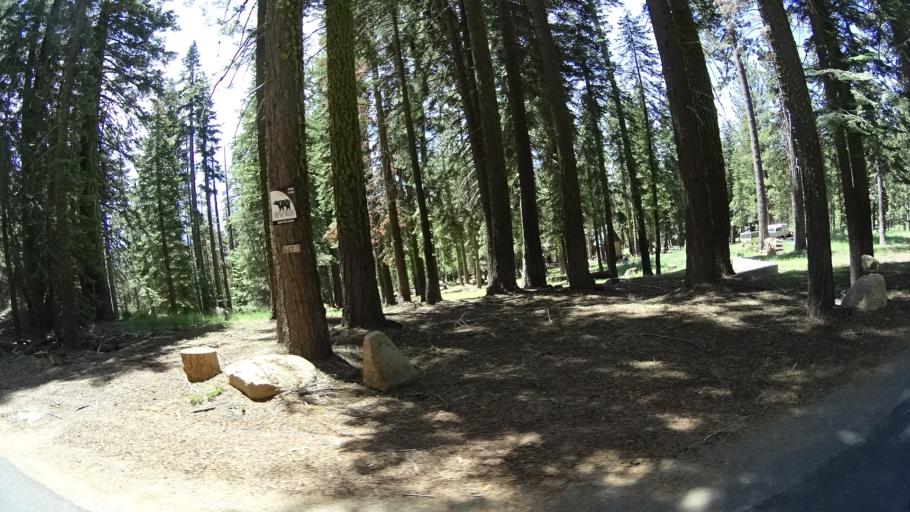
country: US
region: California
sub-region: Calaveras County
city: Arnold
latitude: 38.4279
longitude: -120.0970
